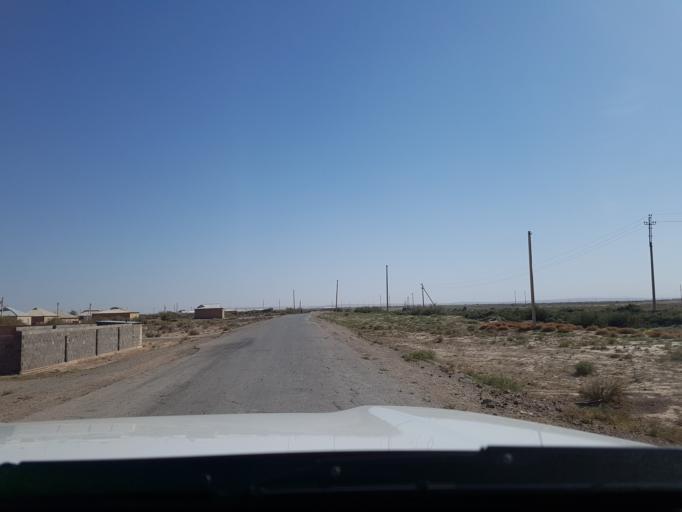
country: IR
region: Razavi Khorasan
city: Sarakhs
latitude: 36.5157
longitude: 61.2524
